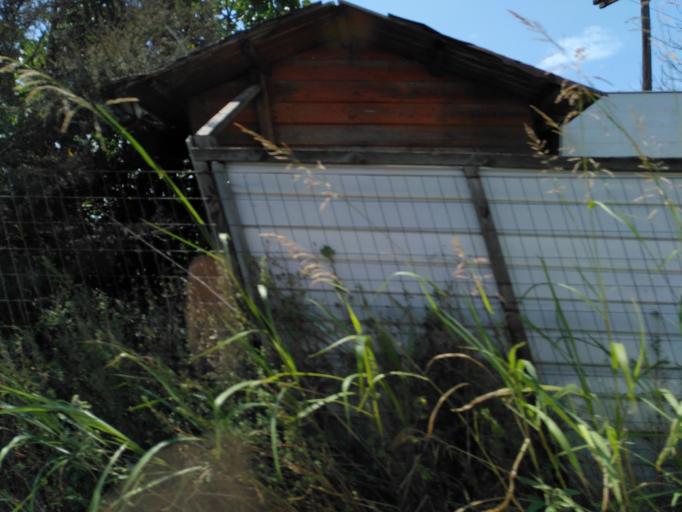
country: GR
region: Central Macedonia
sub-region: Nomos Thessalonikis
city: Agia Triada
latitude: 40.4967
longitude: 22.8491
